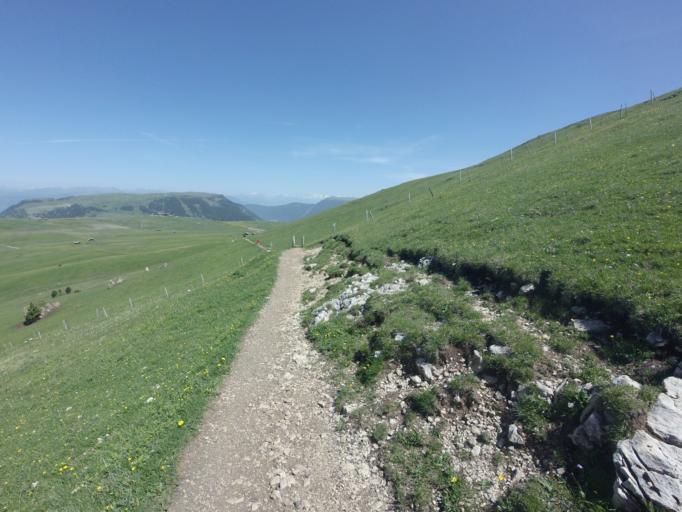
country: IT
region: Trentino-Alto Adige
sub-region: Bolzano
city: Ortisei
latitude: 46.5184
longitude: 11.6325
